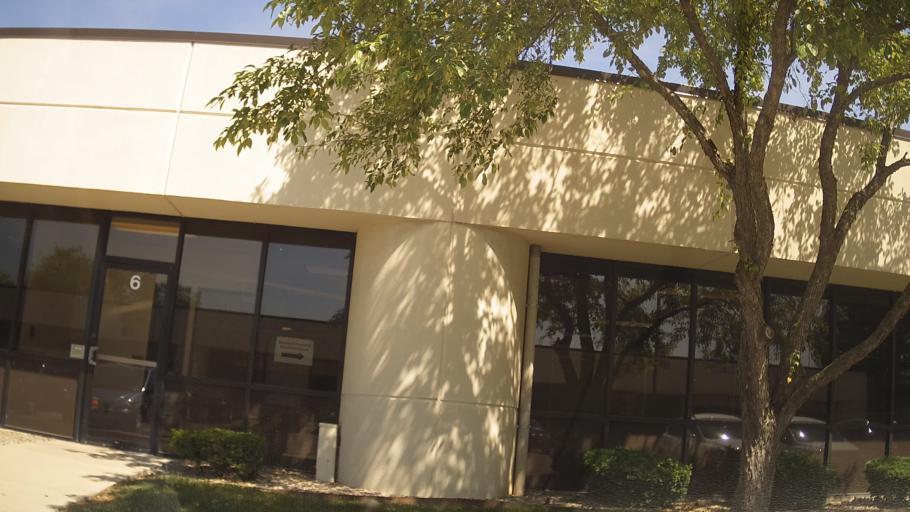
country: US
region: Michigan
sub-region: Wayne County
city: Dearborn
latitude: 42.3072
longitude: -83.1810
